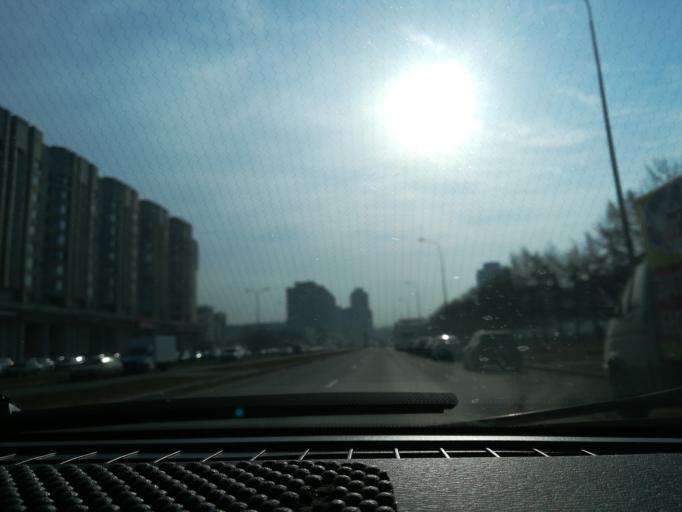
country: RU
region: St.-Petersburg
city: Vasyl'evsky Ostrov
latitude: 59.9491
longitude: 30.2258
